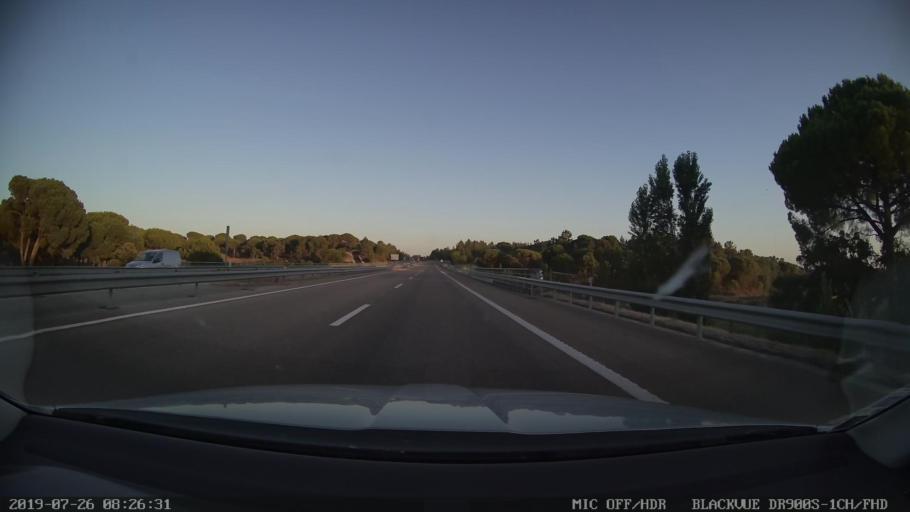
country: PT
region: Evora
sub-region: Vendas Novas
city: Vendas Novas
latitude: 38.6136
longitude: -8.6508
